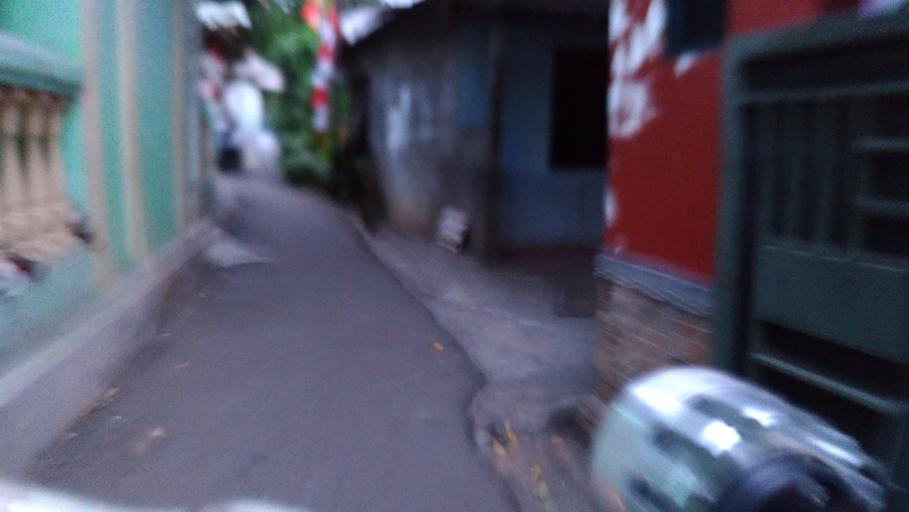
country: ID
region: West Java
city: Depok
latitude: -6.3492
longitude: 106.8709
